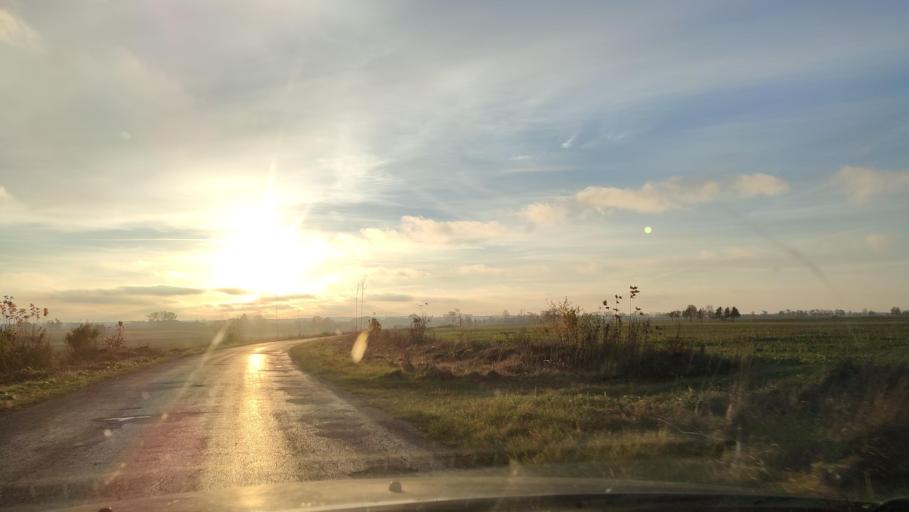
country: PL
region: Masovian Voivodeship
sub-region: Powiat mlawski
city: Wieczfnia Koscielna
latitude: 53.2390
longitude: 20.5735
